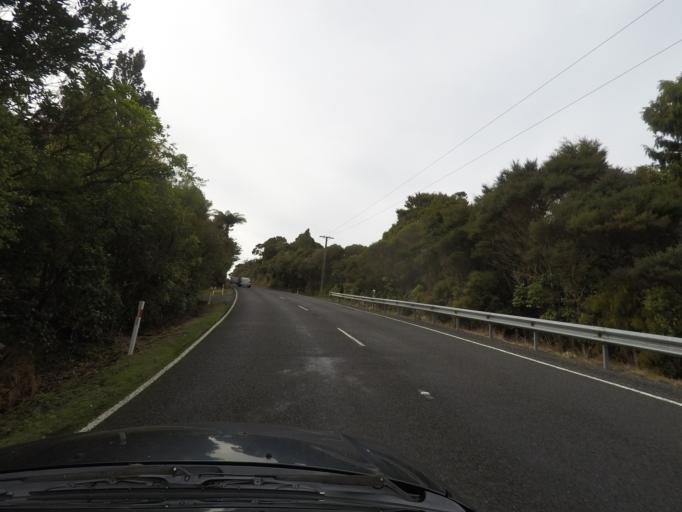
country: NZ
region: Auckland
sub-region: Auckland
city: Titirangi
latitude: -36.9477
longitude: 174.5236
